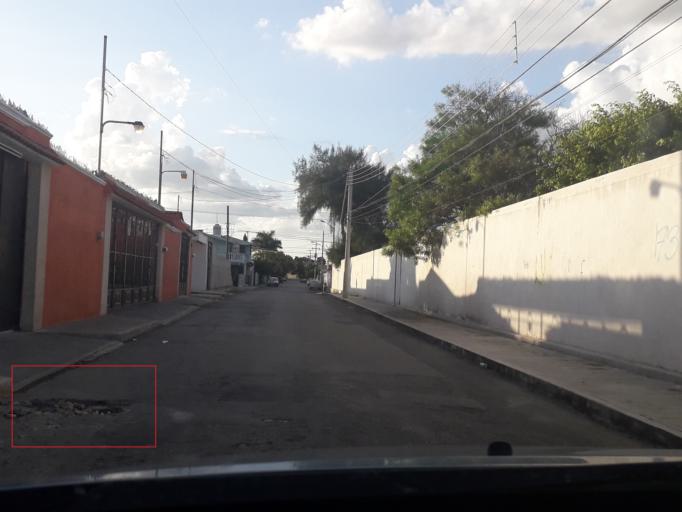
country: MX
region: Yucatan
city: Merida
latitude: 20.9806
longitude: -89.6567
